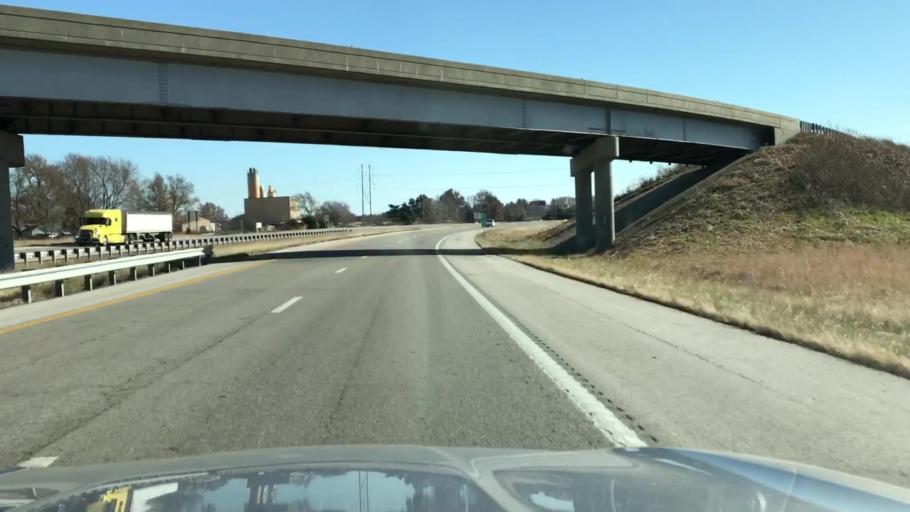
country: US
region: Missouri
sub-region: Jasper County
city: Carthage
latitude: 37.1331
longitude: -94.3140
